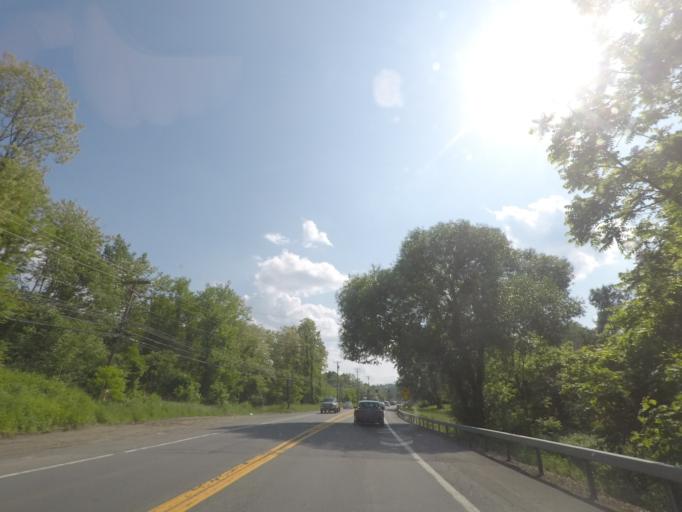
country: US
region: New York
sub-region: Orange County
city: Balmville
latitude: 41.5684
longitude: -73.9947
